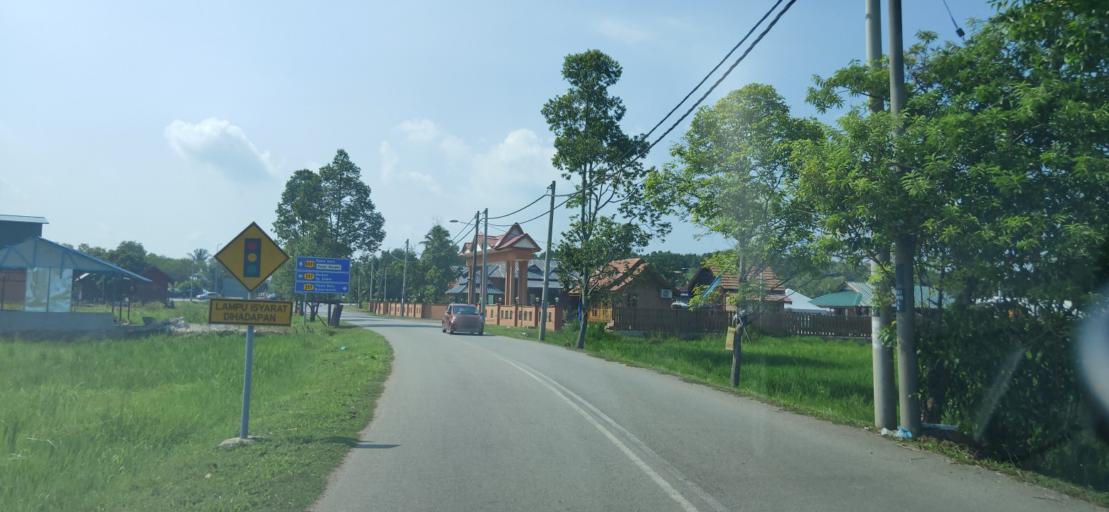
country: MY
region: Kedah
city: Sungai Petani
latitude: 5.6497
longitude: 100.4634
